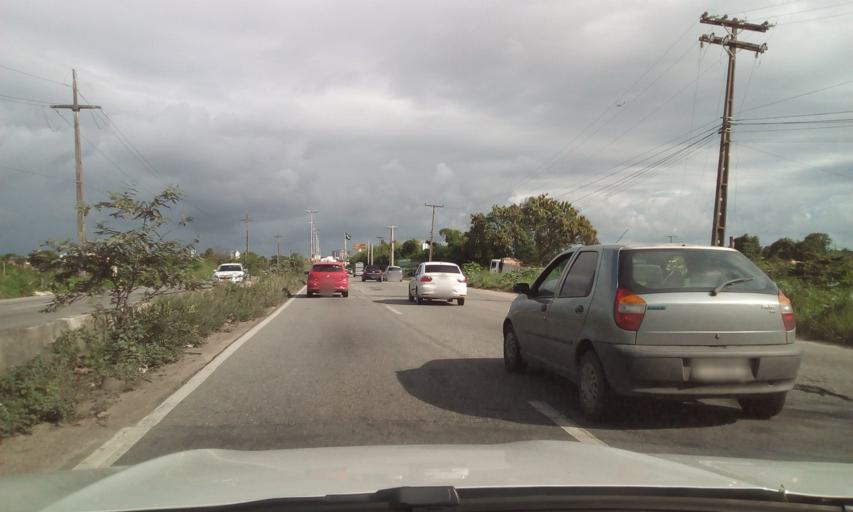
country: BR
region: Pernambuco
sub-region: Recife
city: Recife
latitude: -8.0233
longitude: -34.9428
